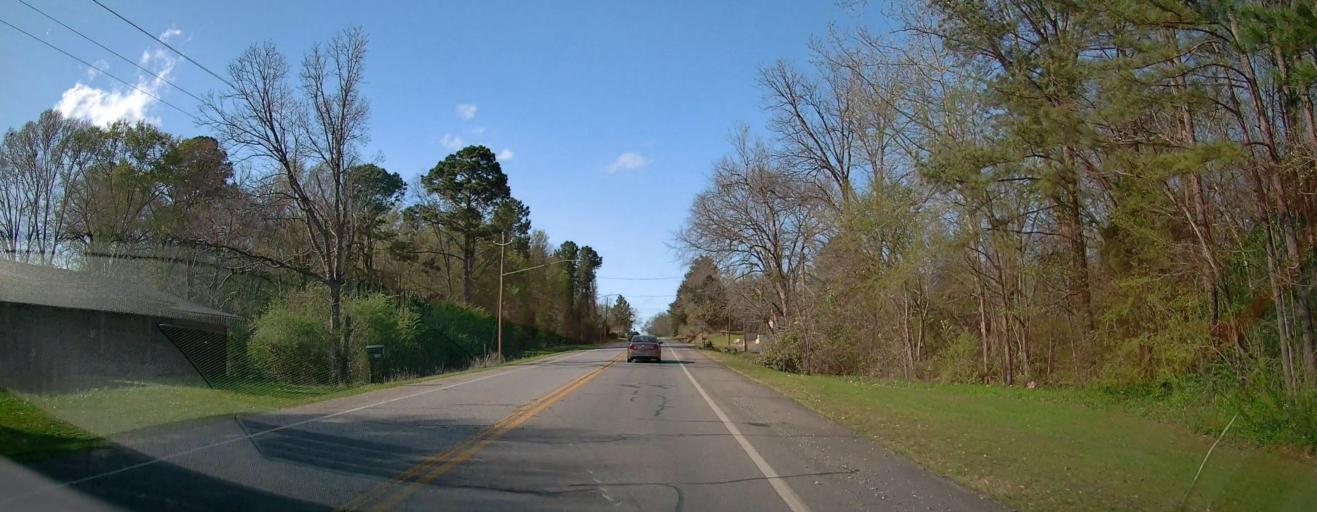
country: US
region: Georgia
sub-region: Baldwin County
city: Milledgeville
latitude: 33.0822
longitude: -83.2448
